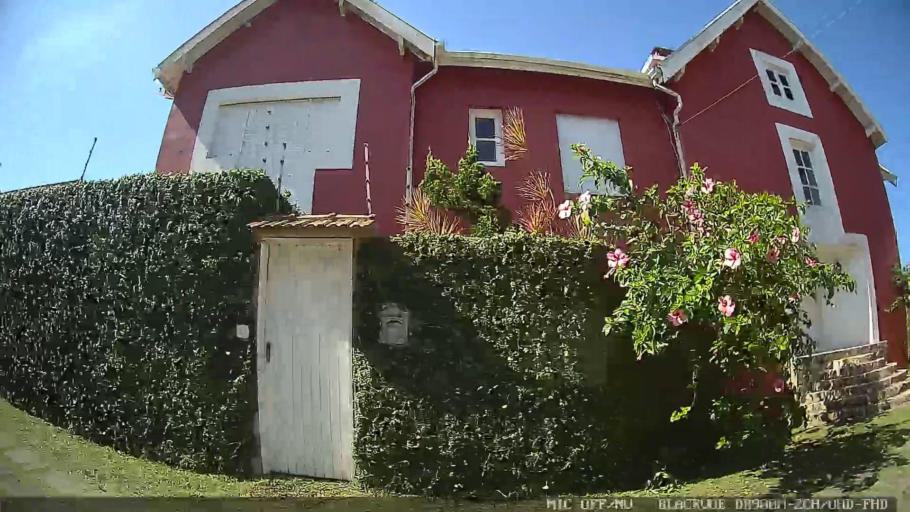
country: BR
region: Sao Paulo
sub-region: Peruibe
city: Peruibe
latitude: -24.2961
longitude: -46.9639
